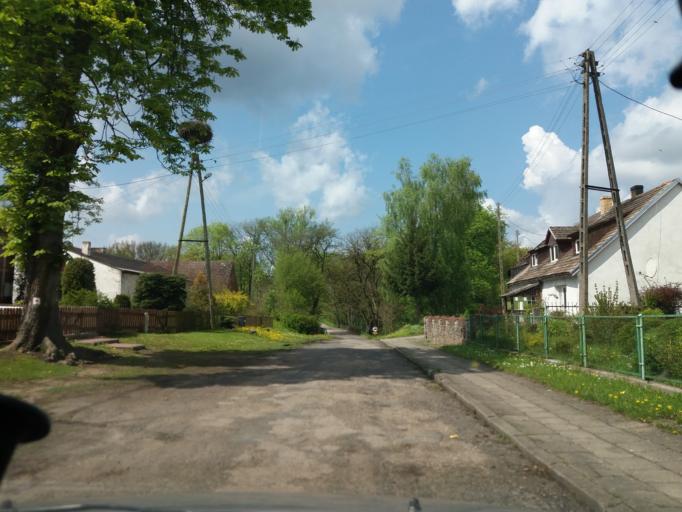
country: PL
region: West Pomeranian Voivodeship
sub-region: Powiat choszczenski
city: Drawno
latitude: 53.1763
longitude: 15.8025
